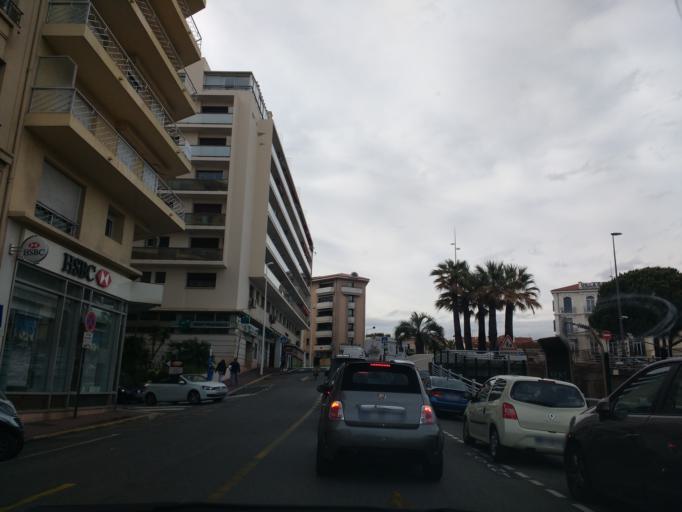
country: FR
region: Provence-Alpes-Cote d'Azur
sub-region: Departement des Alpes-Maritimes
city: Cannes
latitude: 43.5503
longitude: 7.0304
